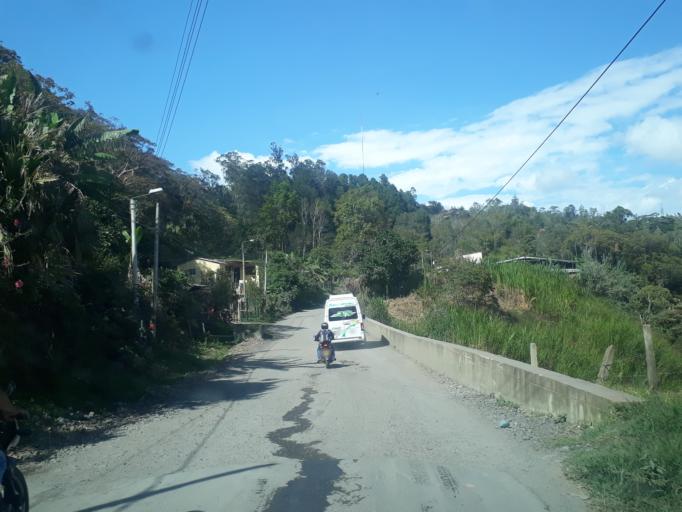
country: CO
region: Santander
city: Velez
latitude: 6.0221
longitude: -73.6693
